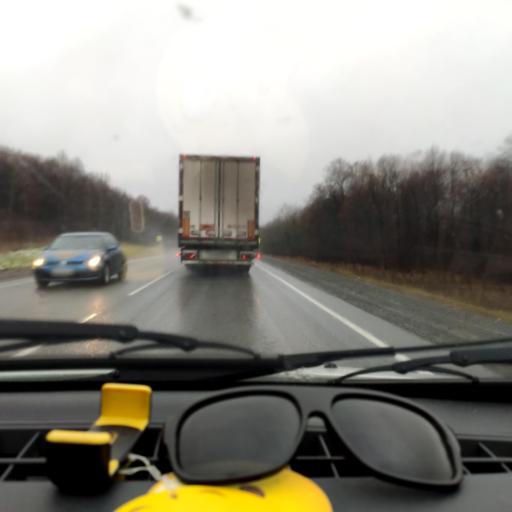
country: RU
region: Bashkortostan
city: Iglino
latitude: 54.7715
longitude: 56.4586
